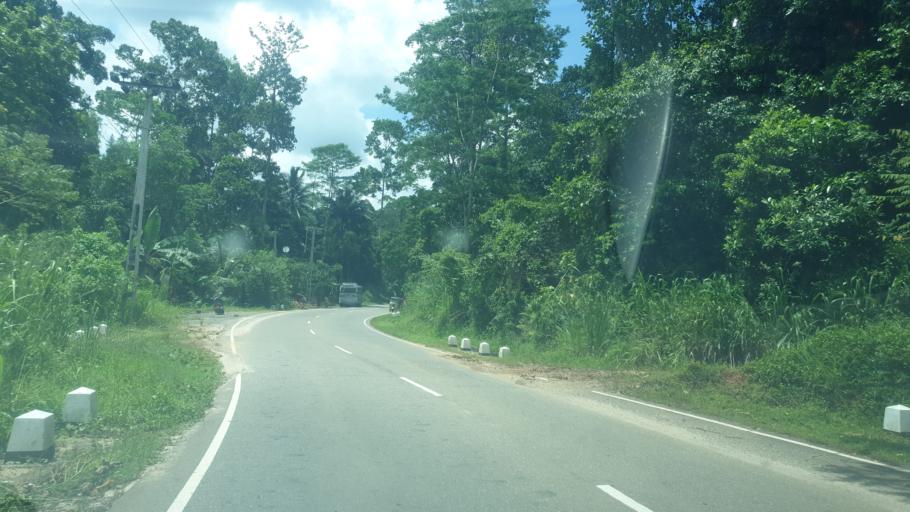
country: LK
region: Western
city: Horawala Junction
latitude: 6.5429
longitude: 80.2762
